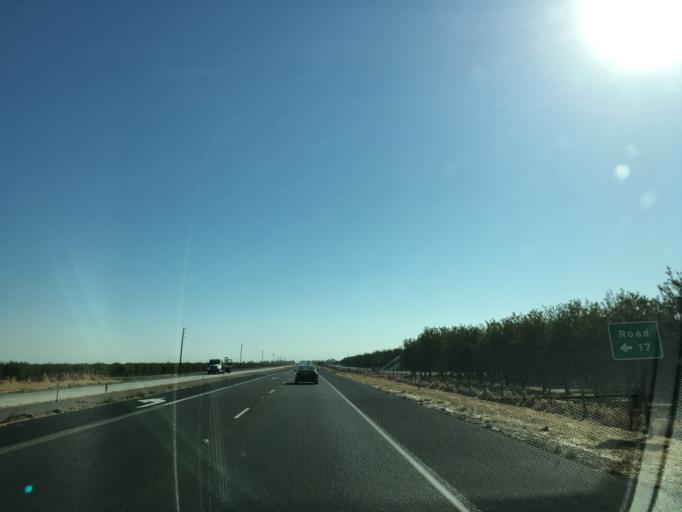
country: US
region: California
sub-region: Madera County
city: Chowchilla
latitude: 37.0838
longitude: -120.2404
